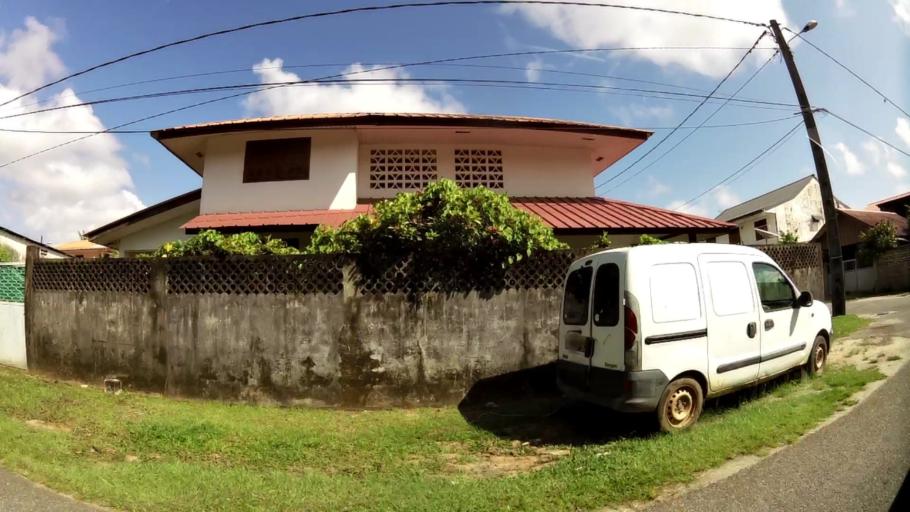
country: GF
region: Guyane
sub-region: Guyane
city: Cayenne
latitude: 4.9384
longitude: -52.3137
